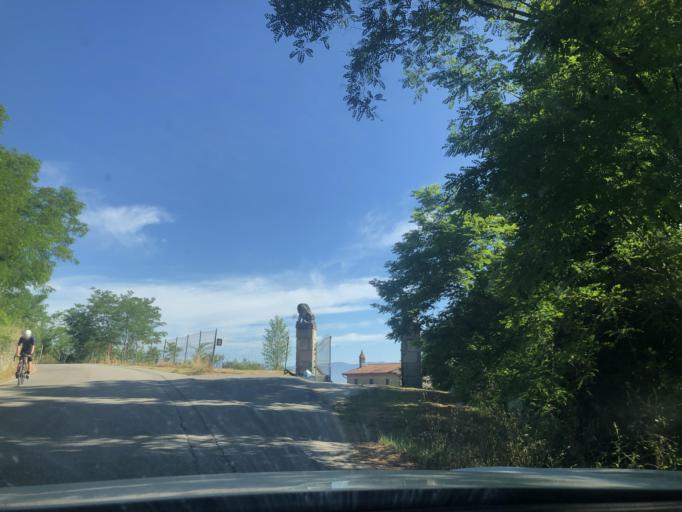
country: IT
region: Tuscany
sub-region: Provincia di Pistoia
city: Larciano
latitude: 43.8414
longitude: 10.9165
